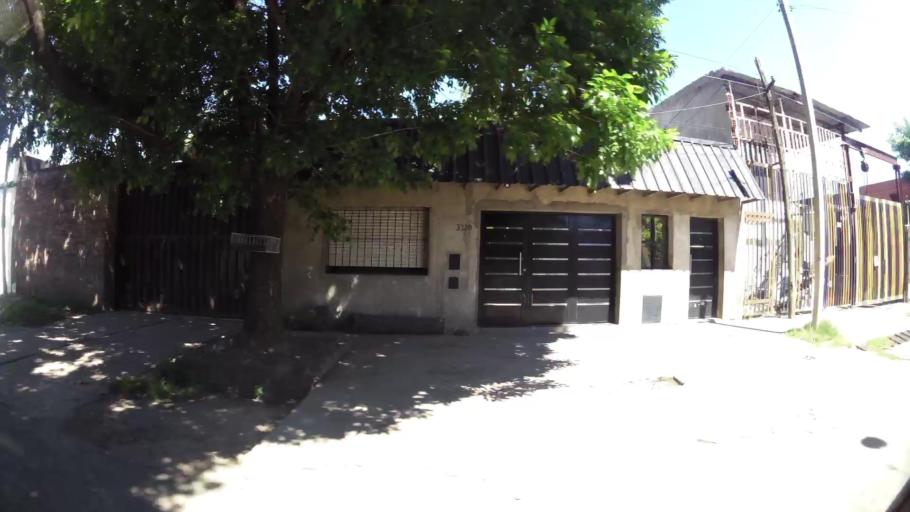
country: AR
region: Santa Fe
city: Perez
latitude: -32.9654
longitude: -60.7154
